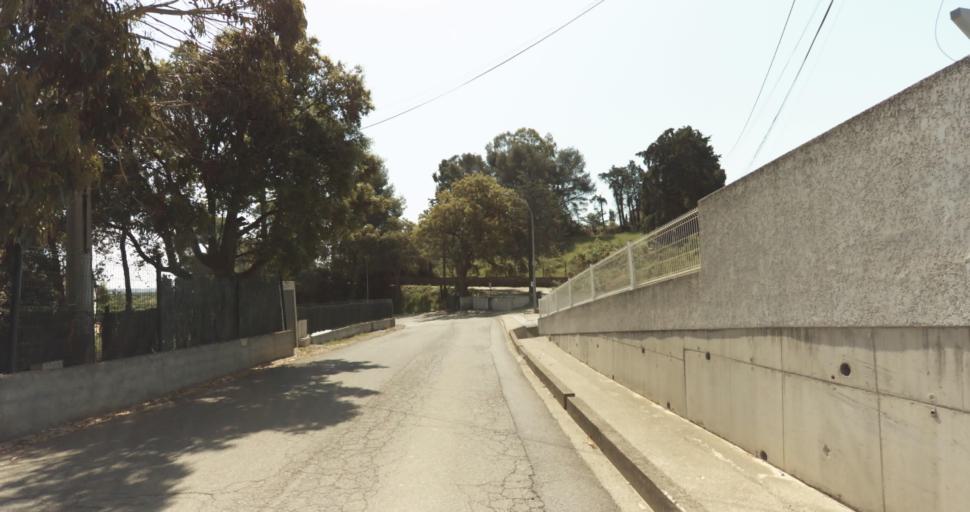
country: FR
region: Corsica
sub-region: Departement de la Haute-Corse
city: Biguglia
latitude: 42.6198
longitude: 9.4315
